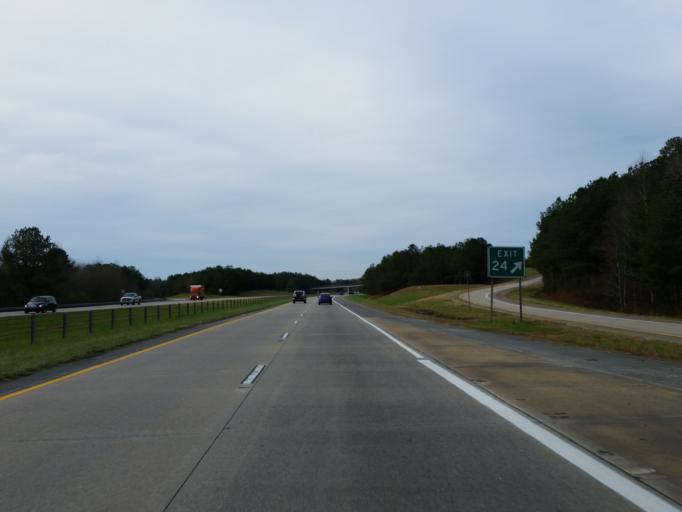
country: US
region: Georgia
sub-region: Cherokee County
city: Ball Ground
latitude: 34.3047
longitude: -84.4188
